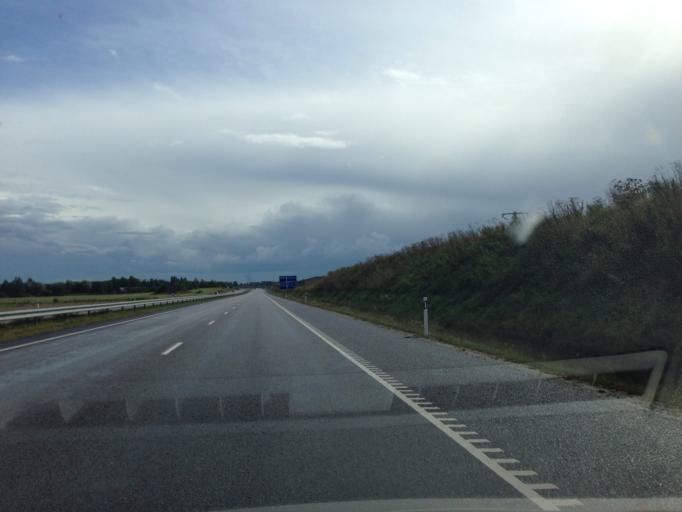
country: EE
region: Jaervamaa
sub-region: Paide linn
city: Paide
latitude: 58.9271
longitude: 25.6132
